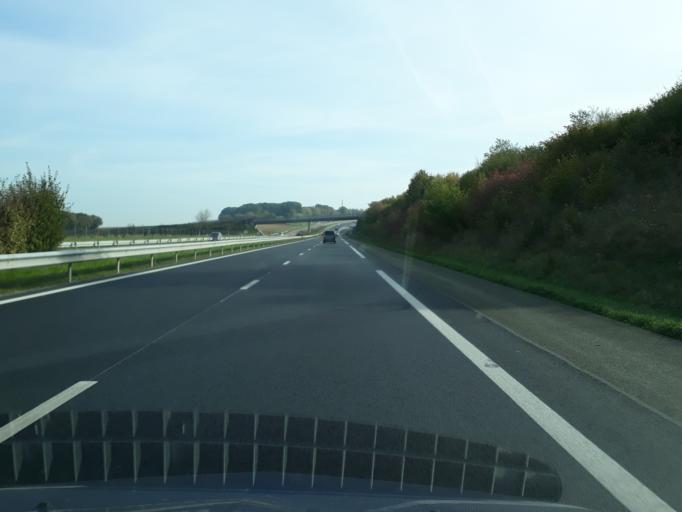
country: FR
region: Bourgogne
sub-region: Departement de l'Yonne
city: Vinneuf
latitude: 48.3714
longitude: 3.1134
